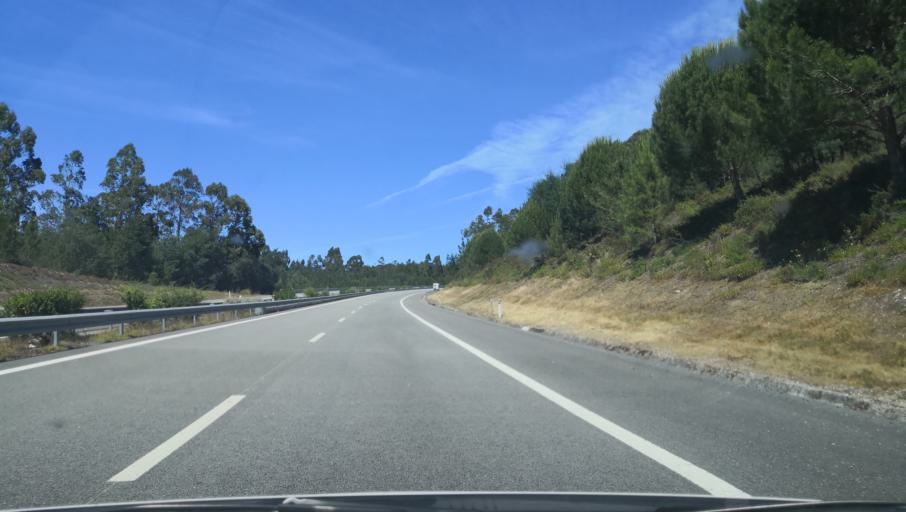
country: PT
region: Coimbra
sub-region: Montemor-O-Velho
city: Arazede
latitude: 40.2440
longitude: -8.6578
